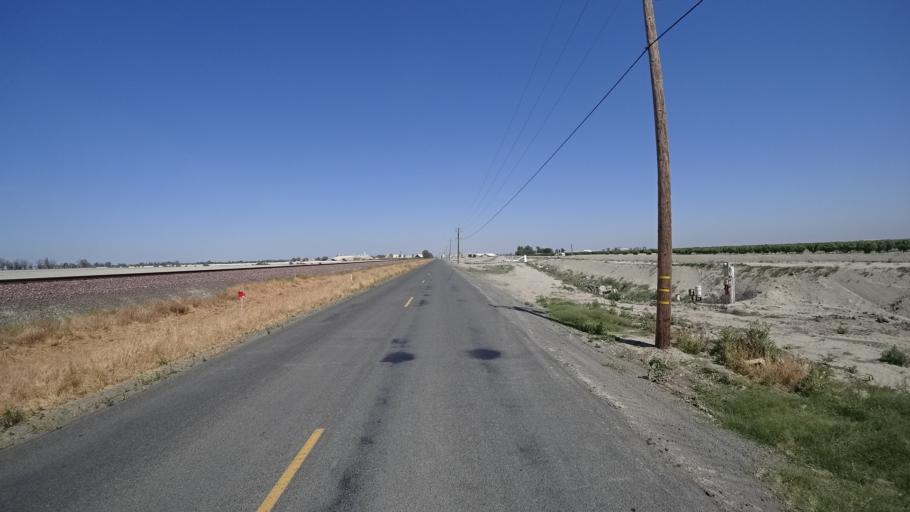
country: US
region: California
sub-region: Kings County
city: Corcoran
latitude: 36.0780
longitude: -119.5418
